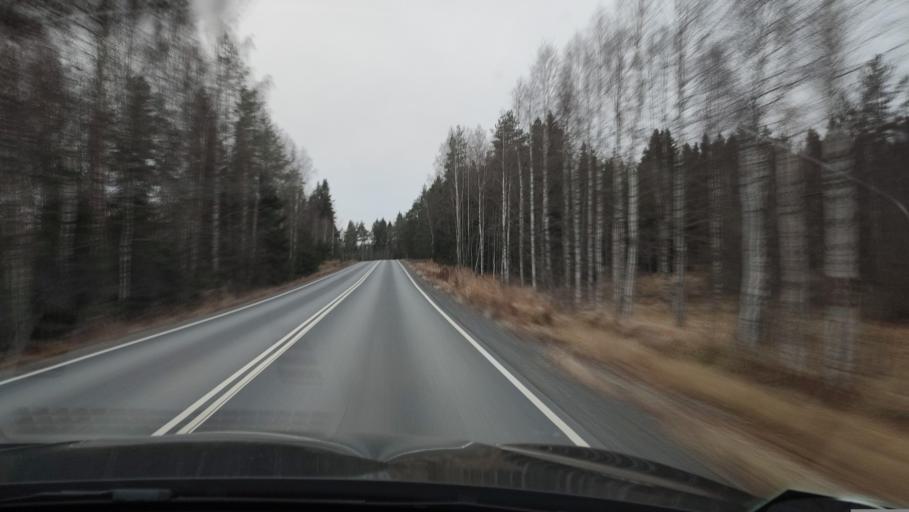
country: FI
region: Southern Ostrobothnia
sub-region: Suupohja
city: Karijoki
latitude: 62.2792
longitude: 21.6077
